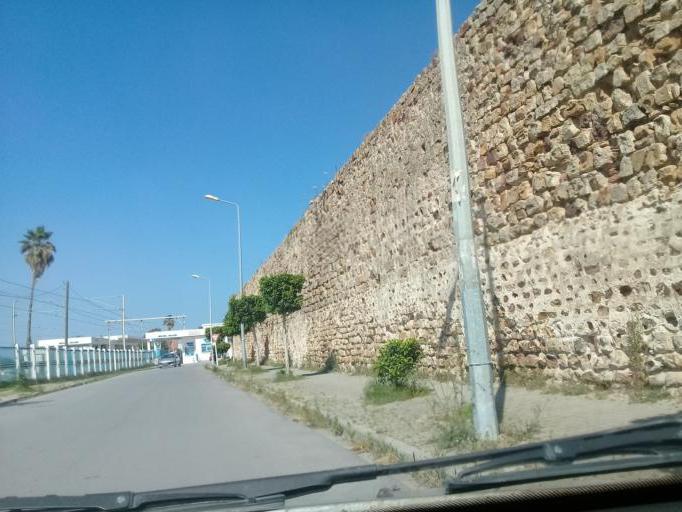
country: TN
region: Tunis
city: La Goulette
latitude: 36.8173
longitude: 10.3007
